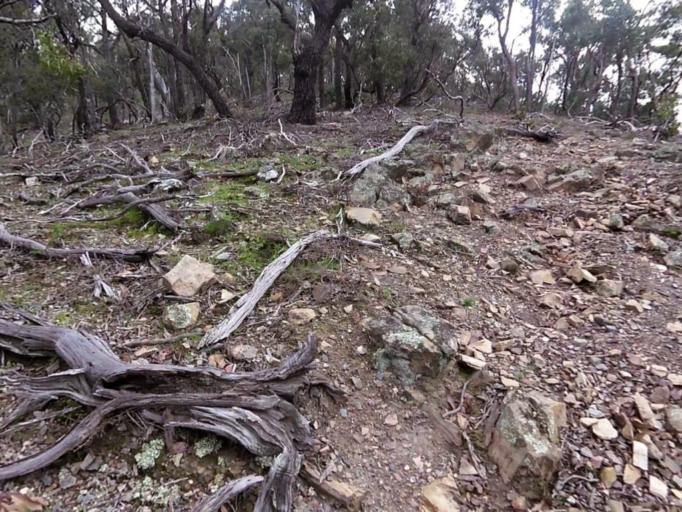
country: AU
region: Victoria
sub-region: Moorabool
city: Bacchus Marsh
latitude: -37.6632
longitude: 144.3461
